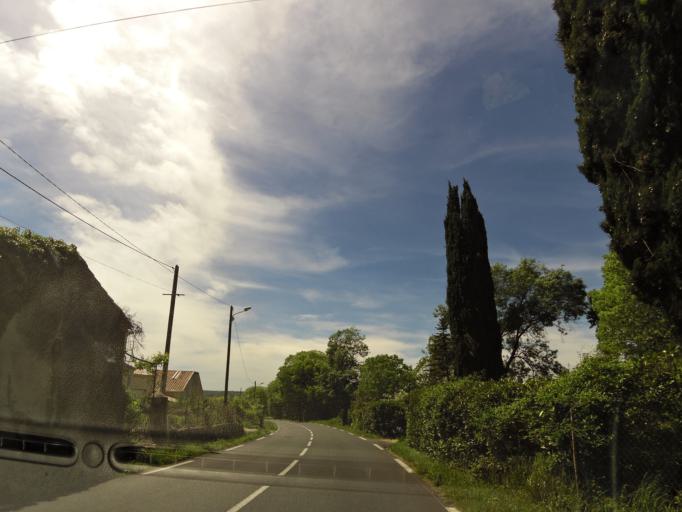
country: FR
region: Languedoc-Roussillon
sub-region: Departement du Gard
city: Villevieille
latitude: 43.7898
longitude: 4.0930
